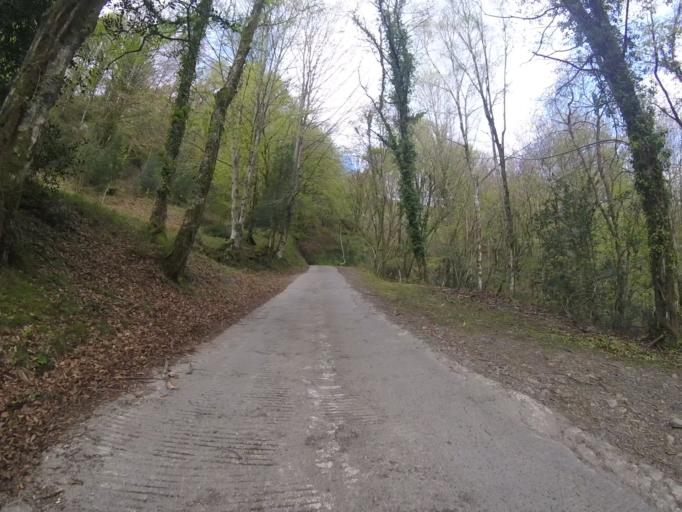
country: ES
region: Basque Country
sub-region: Provincia de Guipuzcoa
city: Errezil
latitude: 43.2013
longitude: -2.1893
